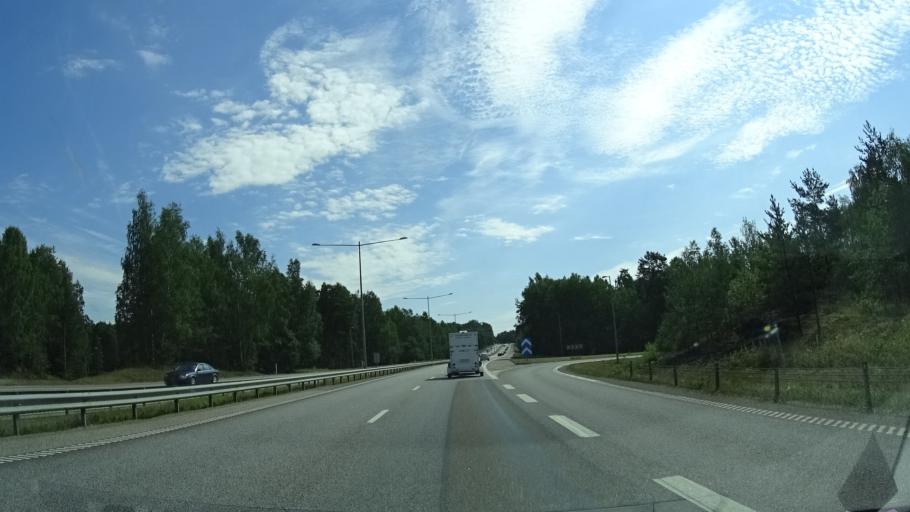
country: SE
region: Vaermland
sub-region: Karlstads Kommun
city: Karlstad
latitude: 59.4013
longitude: 13.5545
